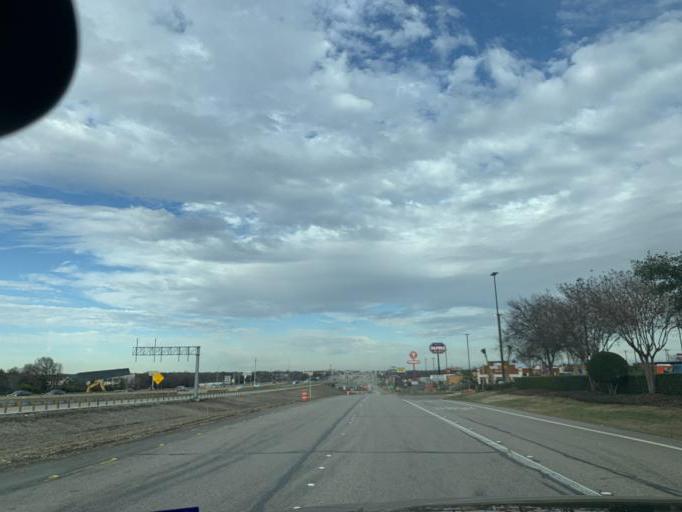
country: US
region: Texas
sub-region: Dallas County
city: Duncanville
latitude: 32.6221
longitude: -96.9109
